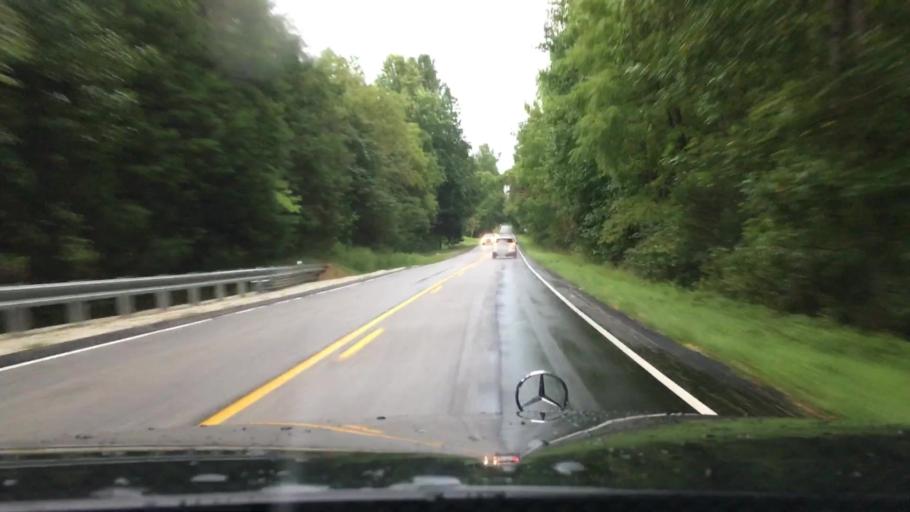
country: US
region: Virginia
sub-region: Amherst County
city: Amherst
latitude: 37.6732
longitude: -79.0143
